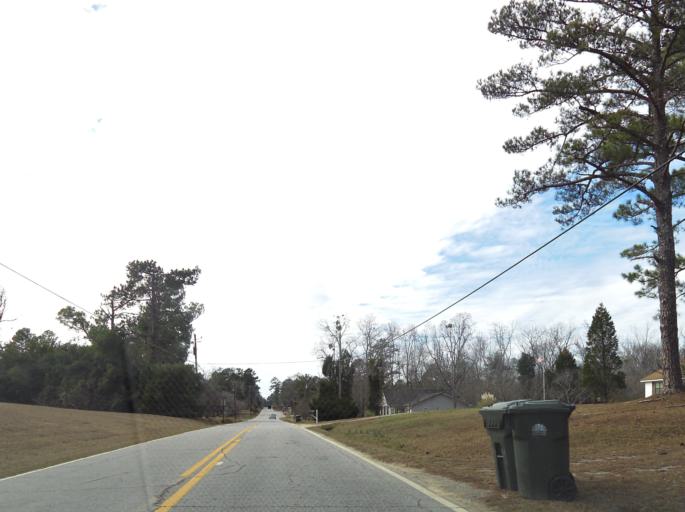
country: US
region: Georgia
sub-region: Bibb County
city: West Point
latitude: 32.8062
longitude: -83.7920
